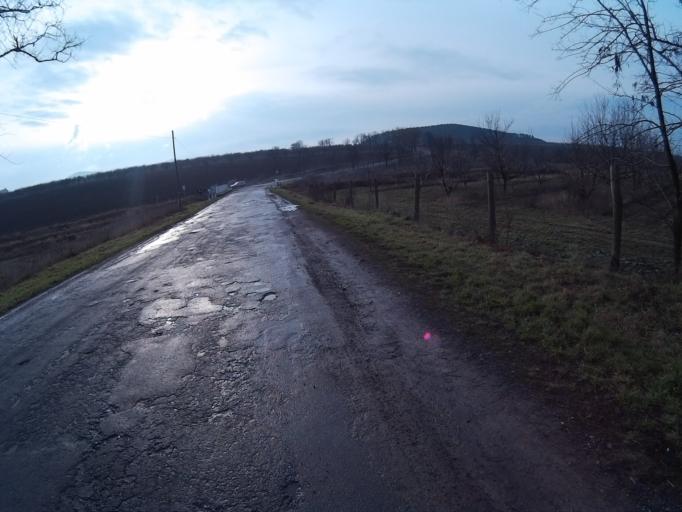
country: HU
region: Borsod-Abauj-Zemplen
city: Abaujszanto
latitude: 48.3458
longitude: 21.2135
